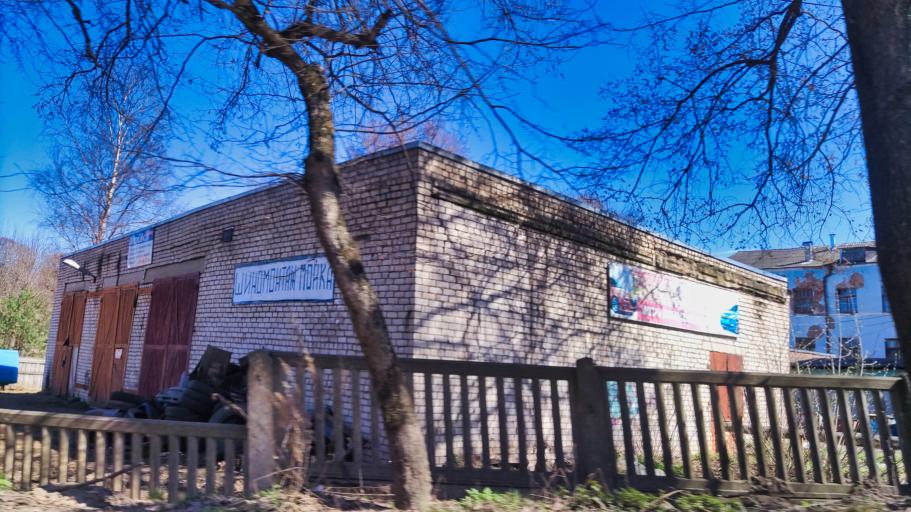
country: RU
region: Tverskaya
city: Rzhev
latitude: 56.2575
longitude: 34.3361
